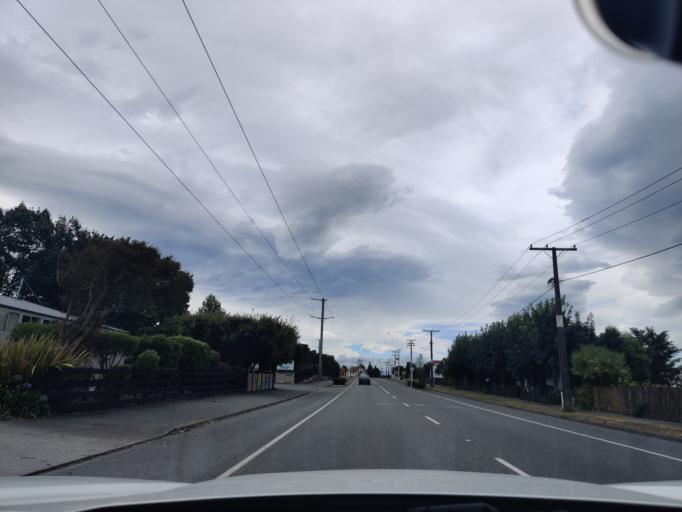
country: NZ
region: Wellington
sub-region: Masterton District
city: Masterton
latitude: -40.9609
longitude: 175.6131
